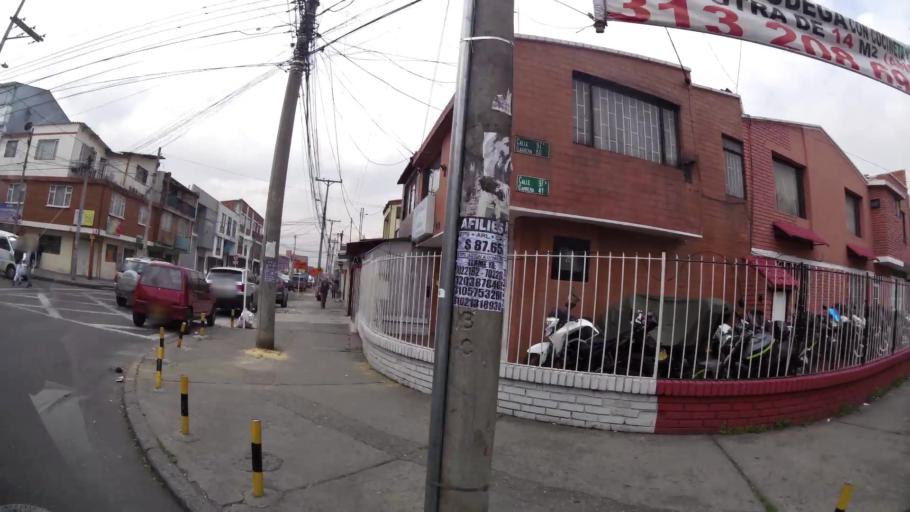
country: CO
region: Bogota D.C.
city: Barrio San Luis
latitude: 4.6865
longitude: -74.0657
